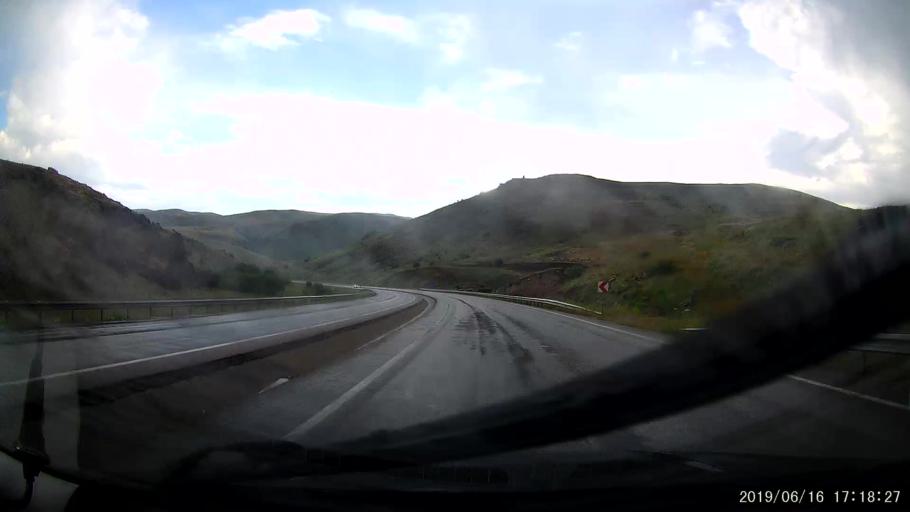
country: TR
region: Erzincan
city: Tercan
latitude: 39.8140
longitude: 40.5287
